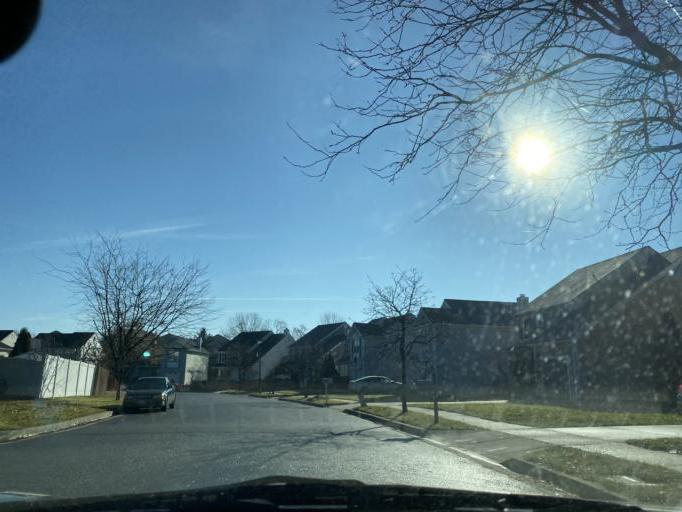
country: US
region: Maryland
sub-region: Prince George's County
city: South Laurel
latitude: 39.0815
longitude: -76.8701
